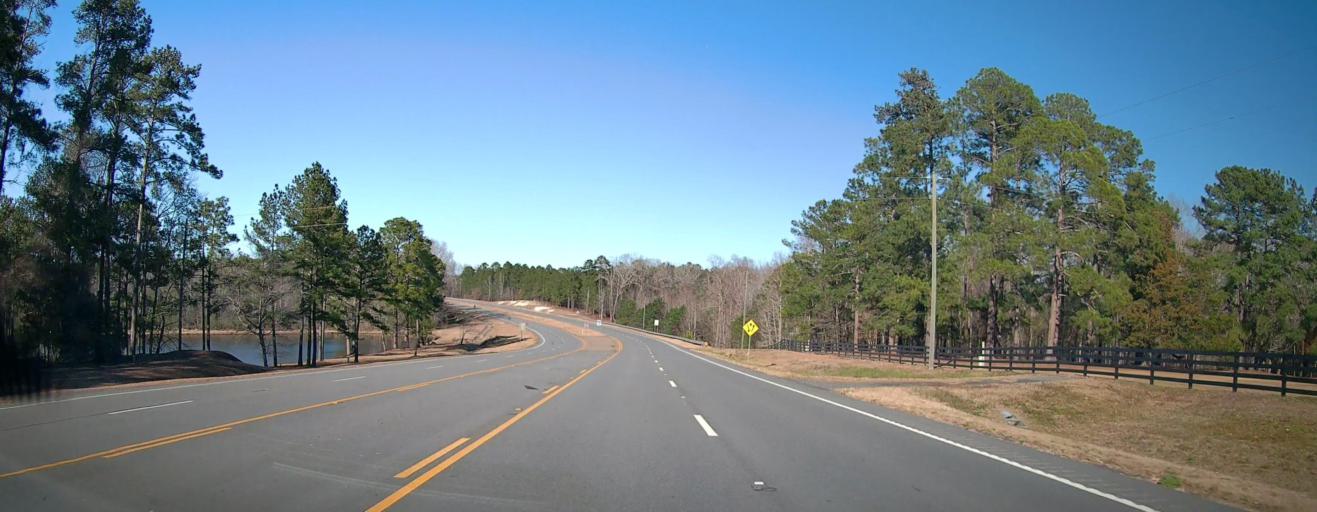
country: US
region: Georgia
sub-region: Taylor County
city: Butler
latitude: 32.5839
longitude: -84.2365
